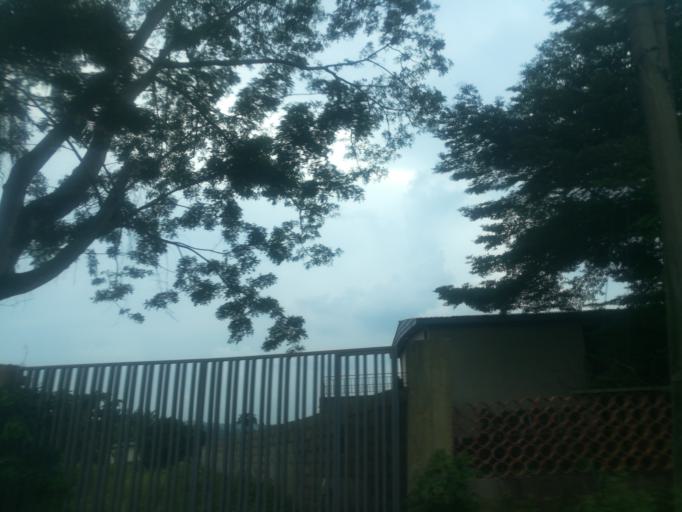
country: NG
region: Oyo
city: Ibadan
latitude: 7.4178
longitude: 3.9043
